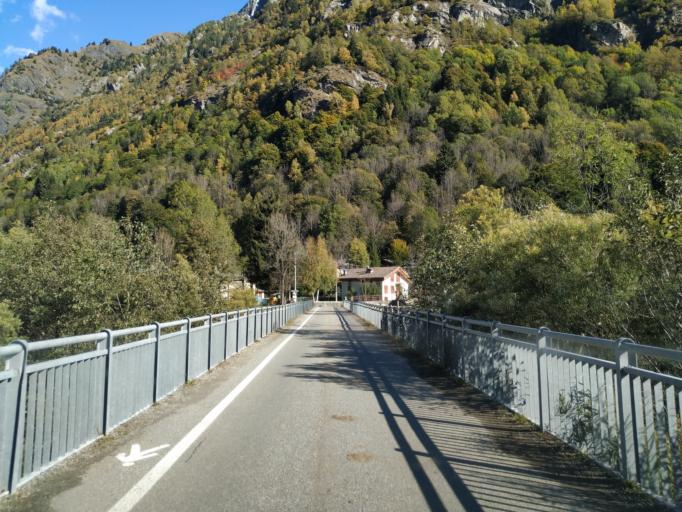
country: IT
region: Piedmont
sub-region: Provincia di Vercelli
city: Riva Valdobbia
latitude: 45.8371
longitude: 7.9517
